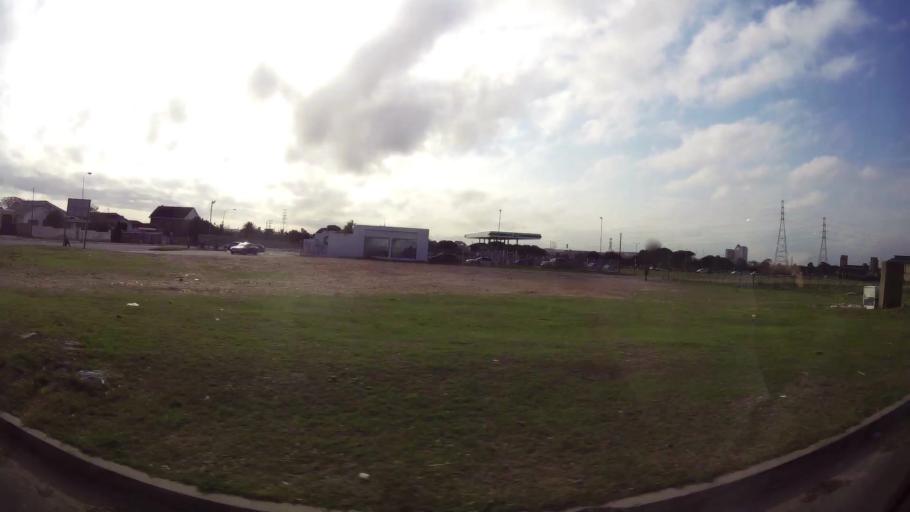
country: ZA
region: Eastern Cape
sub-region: Nelson Mandela Bay Metropolitan Municipality
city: Port Elizabeth
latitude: -33.9202
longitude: 25.5636
